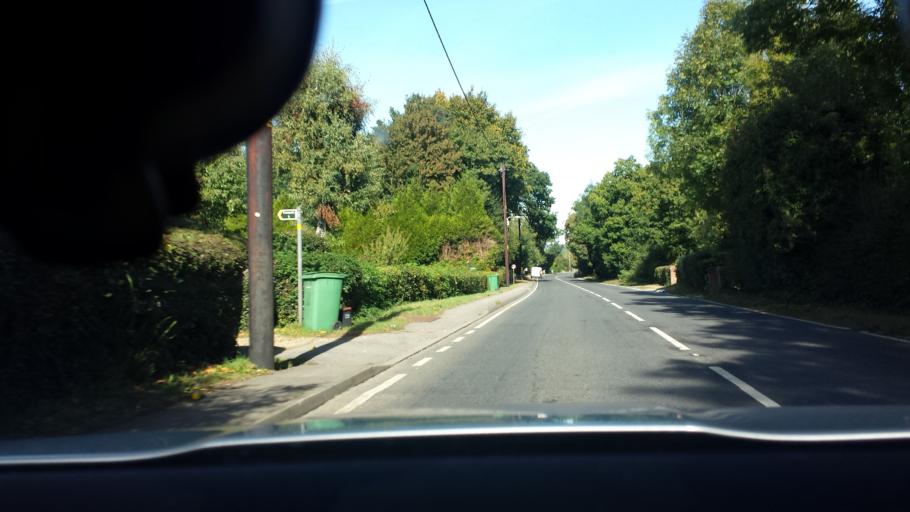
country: GB
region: England
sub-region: Kent
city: Staplehurst
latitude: 51.1757
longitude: 0.5524
